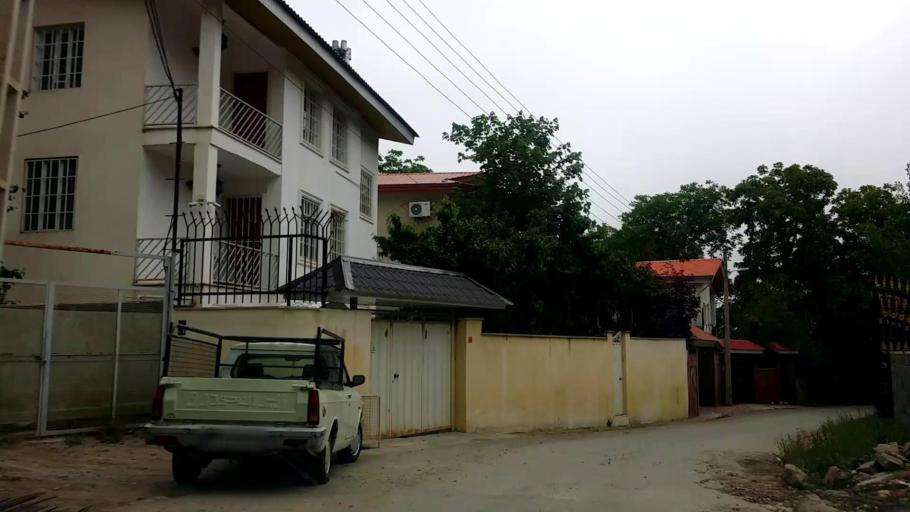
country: IR
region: Mazandaran
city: `Abbasabad
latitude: 36.4983
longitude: 51.1414
